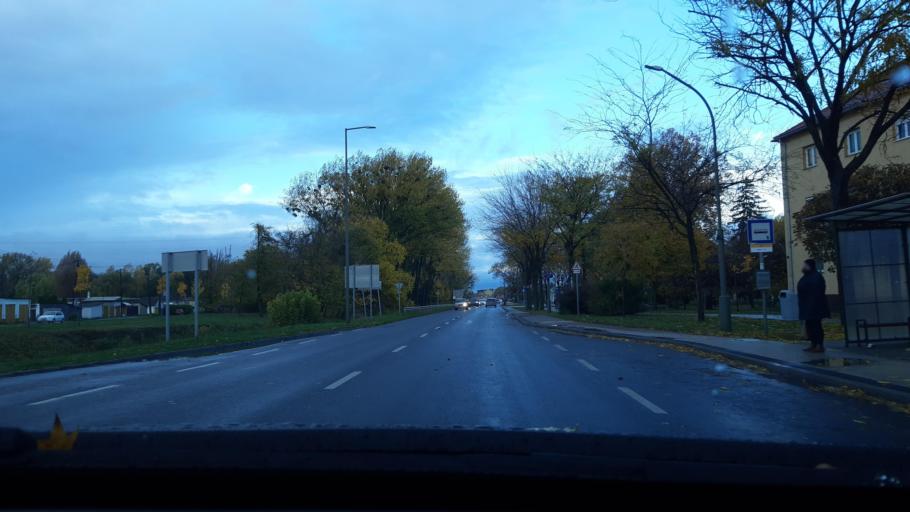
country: HU
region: Veszprem
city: Ajka
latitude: 47.1038
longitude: 17.5551
